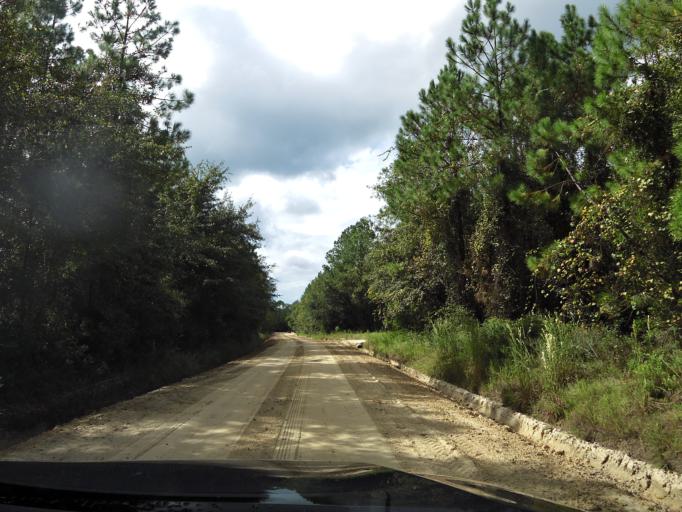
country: US
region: Florida
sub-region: Nassau County
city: Hilliard
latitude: 30.6063
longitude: -82.0727
